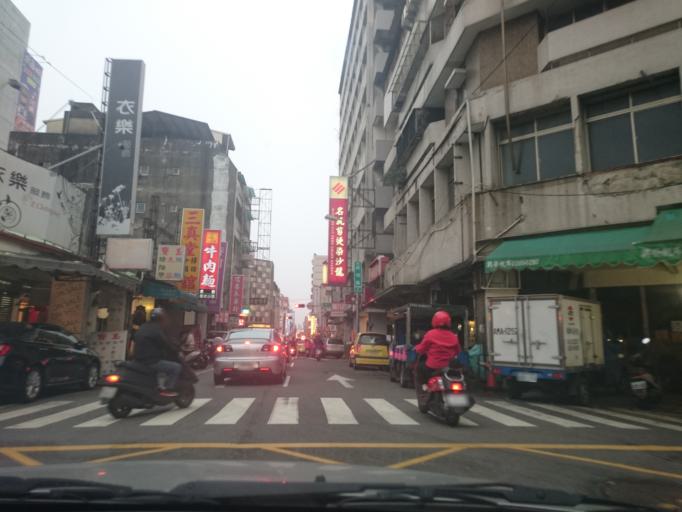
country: TW
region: Taiwan
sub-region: Taichung City
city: Taichung
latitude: 24.1462
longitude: 120.6768
